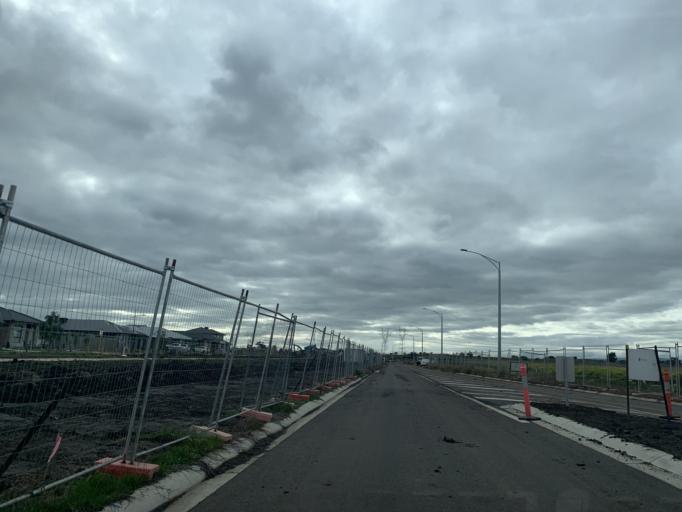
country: AU
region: Victoria
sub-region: Hume
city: Craigieburn
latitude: -37.5989
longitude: 145.0003
